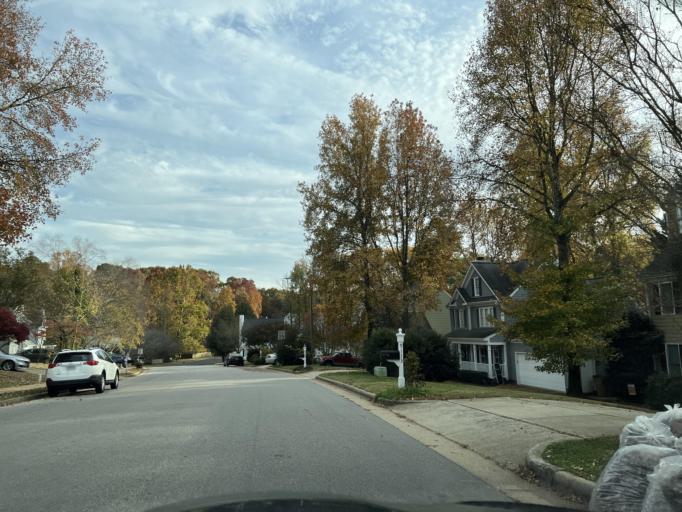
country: US
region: North Carolina
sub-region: Wake County
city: Wake Forest
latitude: 35.9020
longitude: -78.5935
